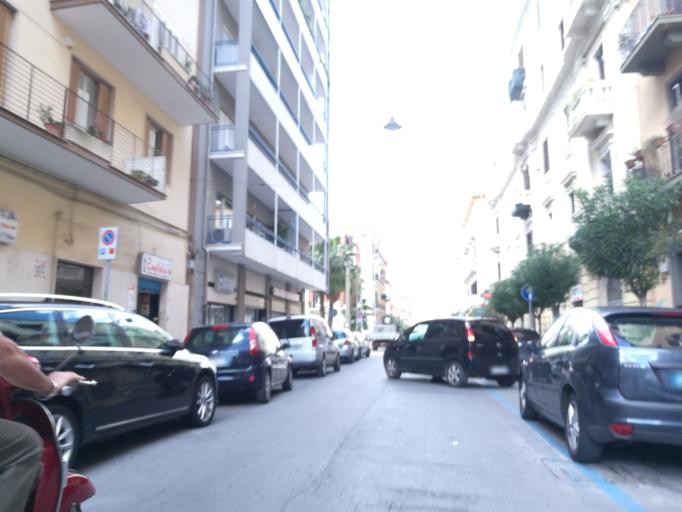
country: IT
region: Apulia
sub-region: Provincia di Bari
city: Bari
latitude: 41.1187
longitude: 16.8838
